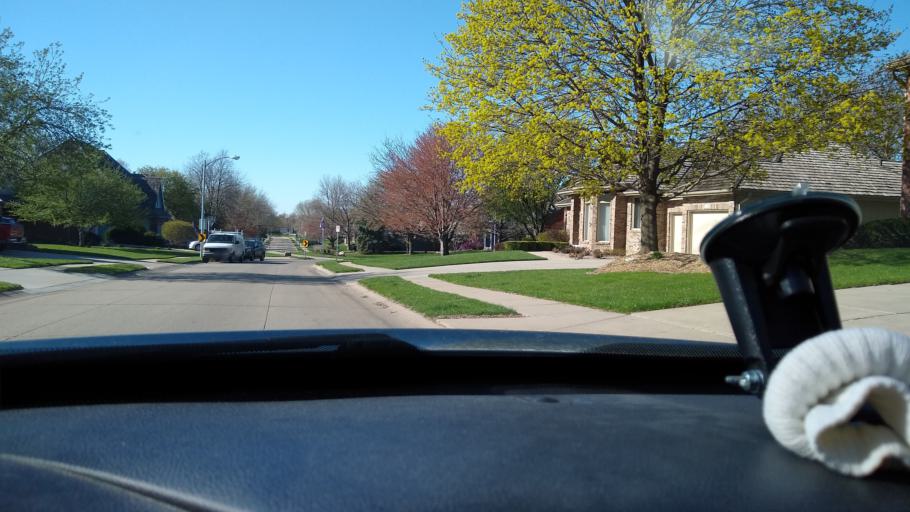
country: US
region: Nebraska
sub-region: Douglas County
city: Ralston
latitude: 41.1953
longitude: -96.0723
